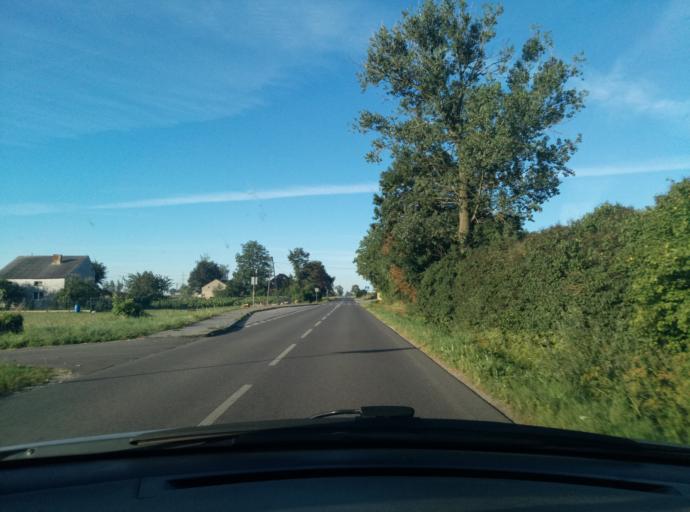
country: PL
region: Kujawsko-Pomorskie
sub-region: Powiat golubsko-dobrzynski
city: Kowalewo Pomorskie
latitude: 53.1892
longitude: 18.9104
